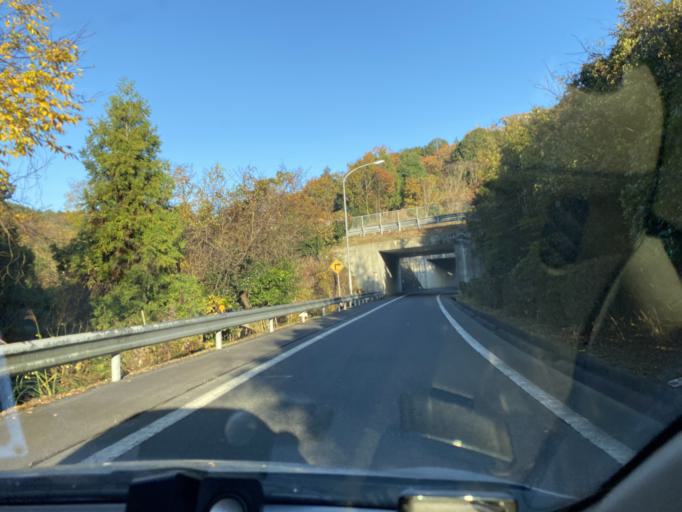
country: JP
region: Kyoto
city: Uji
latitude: 34.9196
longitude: 135.8801
